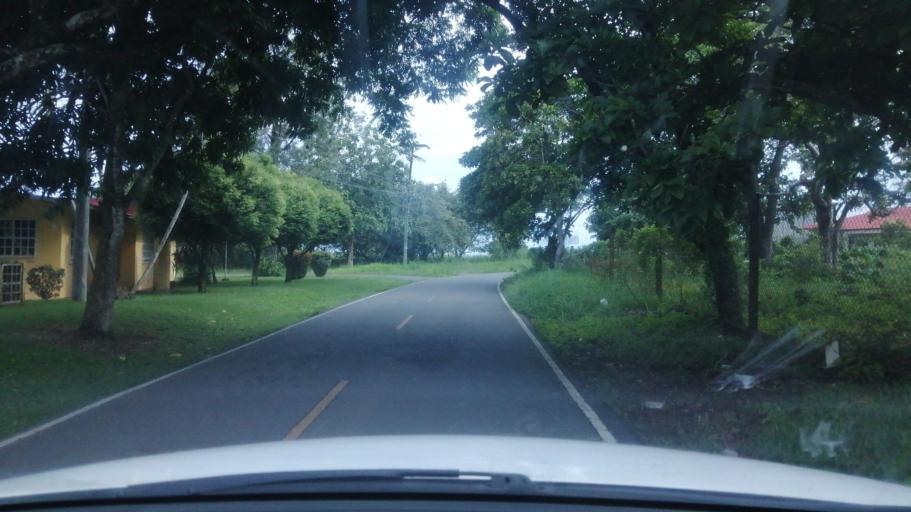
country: PA
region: Chiriqui
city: David
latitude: 8.4024
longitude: -82.4280
